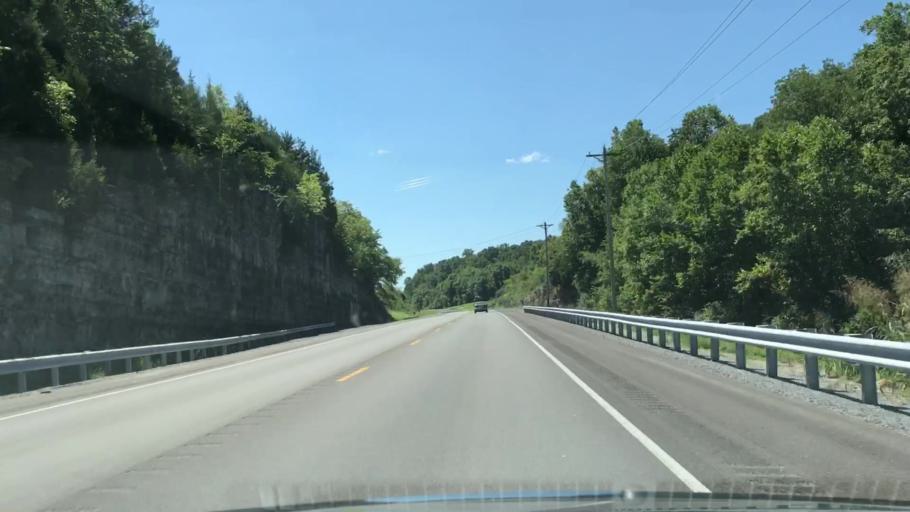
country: US
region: Kentucky
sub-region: Cumberland County
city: Burkesville
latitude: 36.7731
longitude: -85.3781
